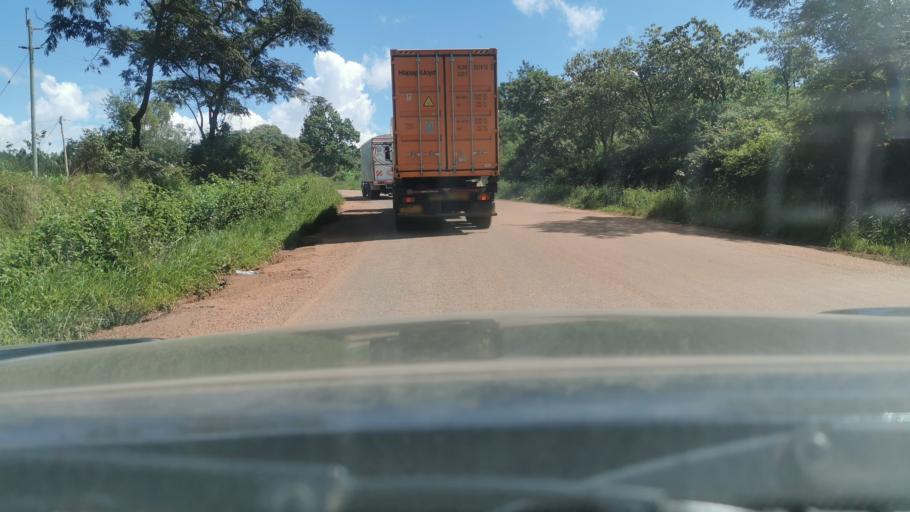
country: TZ
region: Kagera
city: Ngara
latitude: -2.3838
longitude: 30.7909
